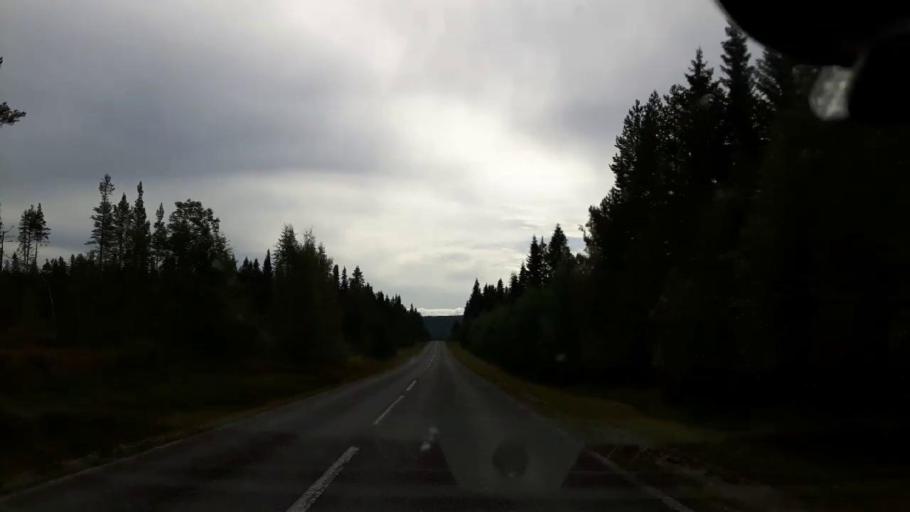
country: SE
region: Jaemtland
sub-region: Ragunda Kommun
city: Hammarstrand
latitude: 63.0569
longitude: 15.9270
